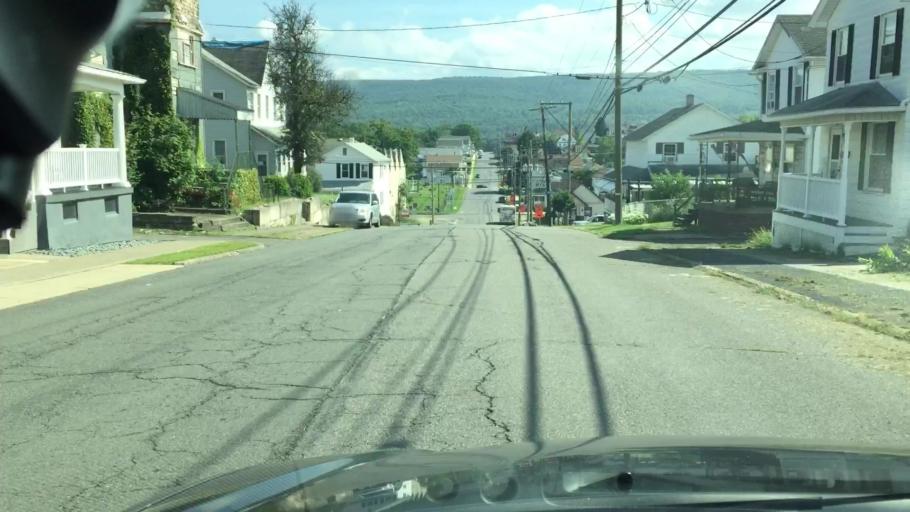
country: US
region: Pennsylvania
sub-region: Luzerne County
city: Nanticoke
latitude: 41.1985
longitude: -75.9997
